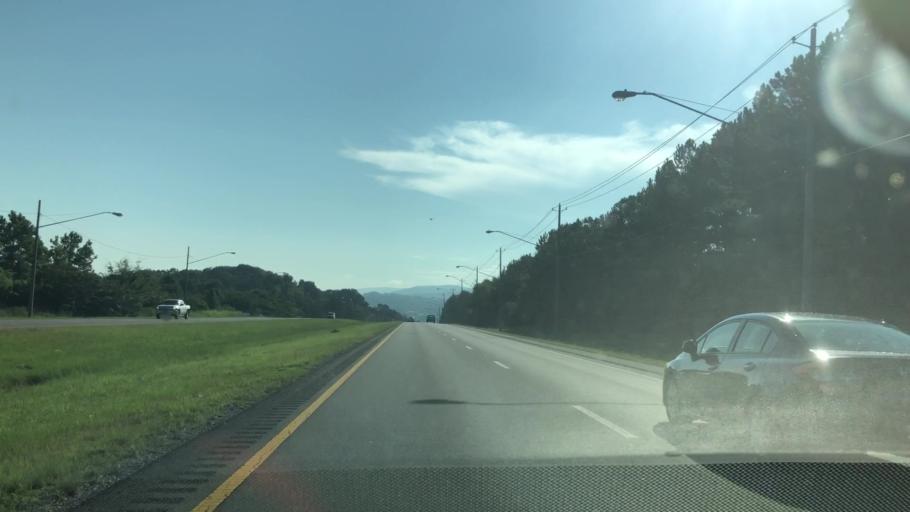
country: US
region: Alabama
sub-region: Calhoun County
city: Anniston
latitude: 33.6523
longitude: -85.8448
